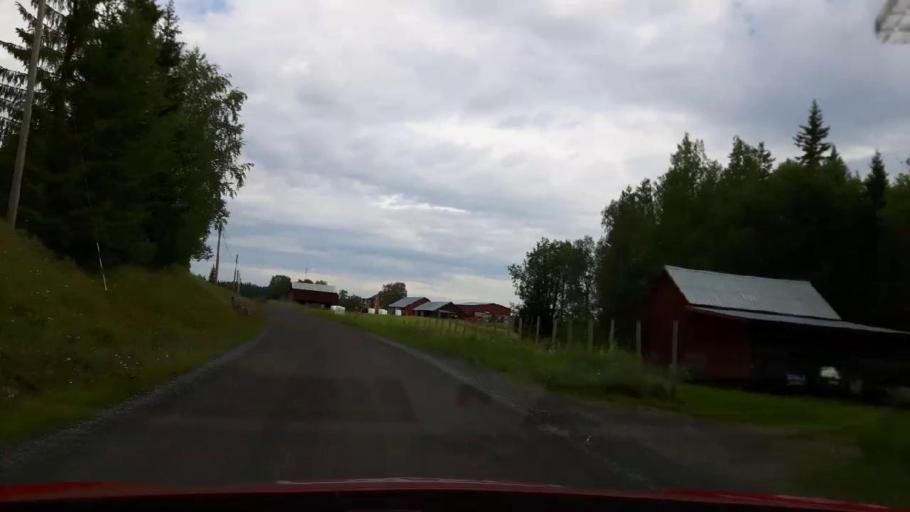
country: SE
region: Jaemtland
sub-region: Stroemsunds Kommun
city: Stroemsund
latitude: 63.4554
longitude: 15.2800
